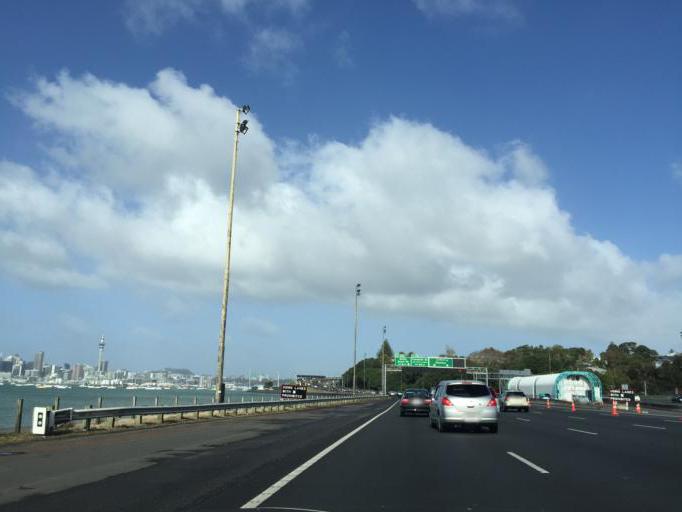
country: NZ
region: Auckland
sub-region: Auckland
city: North Shore
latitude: -36.8179
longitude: 174.7506
